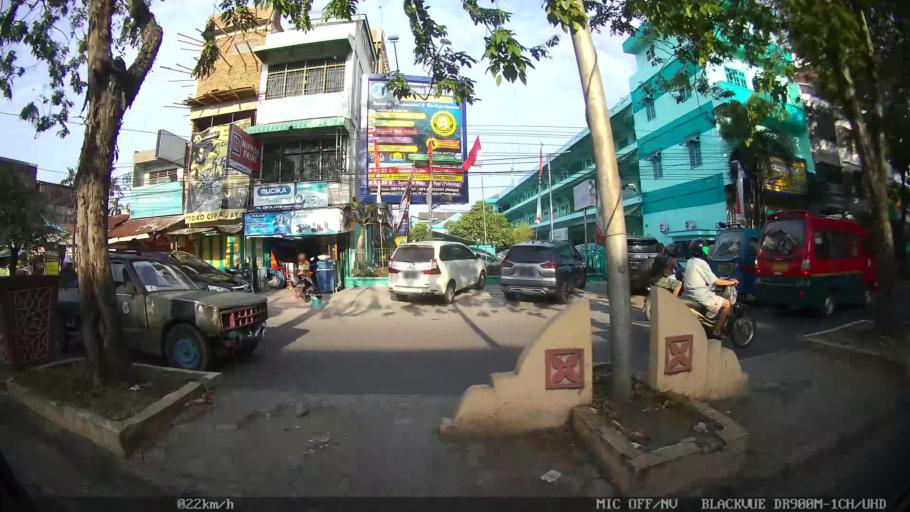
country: ID
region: North Sumatra
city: Medan
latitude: 3.5762
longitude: 98.6430
